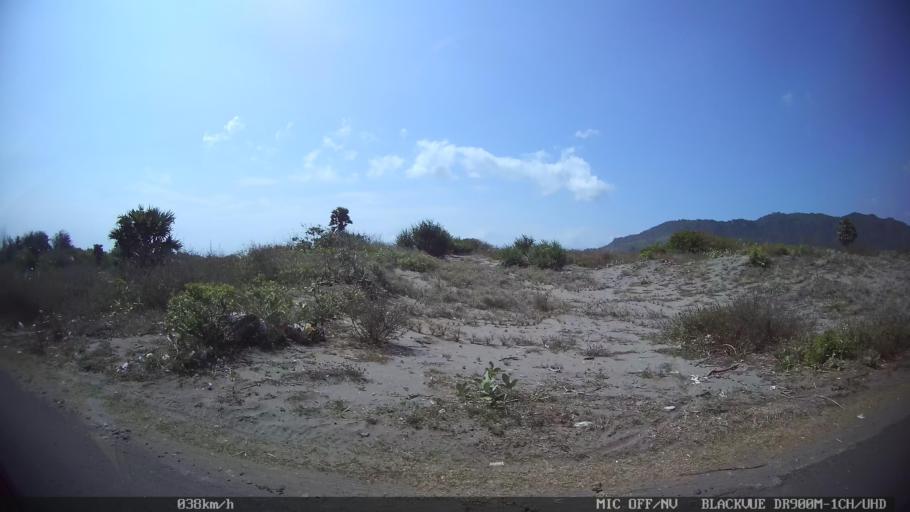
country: ID
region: Daerah Istimewa Yogyakarta
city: Bambanglipuro
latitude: -8.0175
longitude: 110.3104
